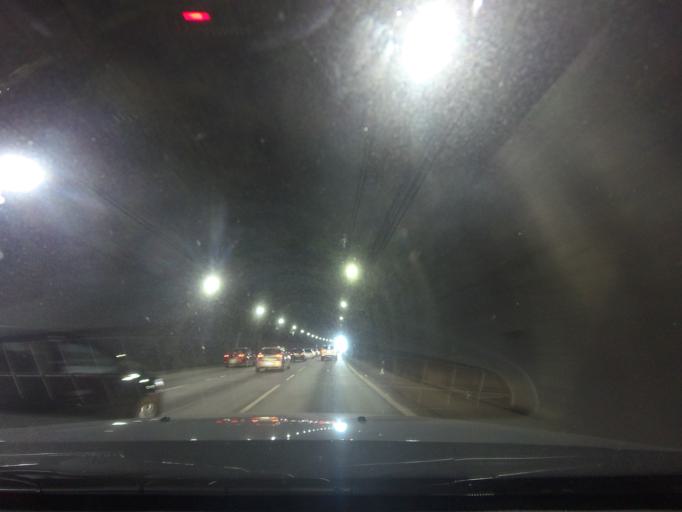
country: BR
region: Sao Paulo
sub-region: Cubatao
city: Cubatao
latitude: -23.9063
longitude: -46.5046
